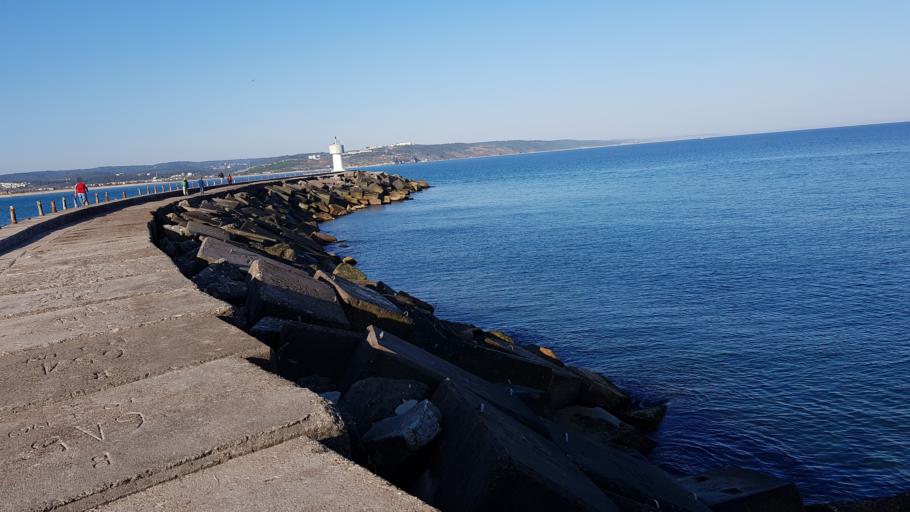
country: TR
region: Istanbul
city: Sile
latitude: 41.1792
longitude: 29.6023
